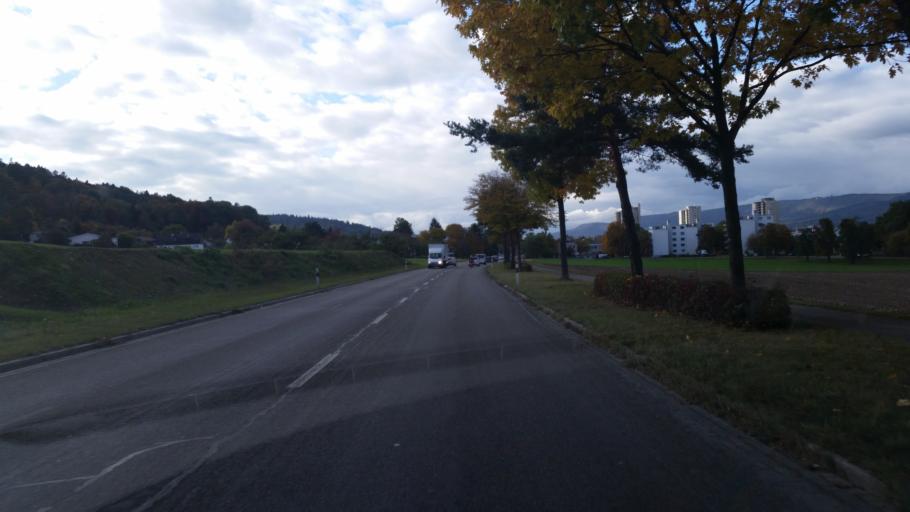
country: CH
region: Zurich
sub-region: Bezirk Zuerich
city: Zuerich (Kreis 10) / Ruetihof
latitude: 47.4260
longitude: 8.4789
